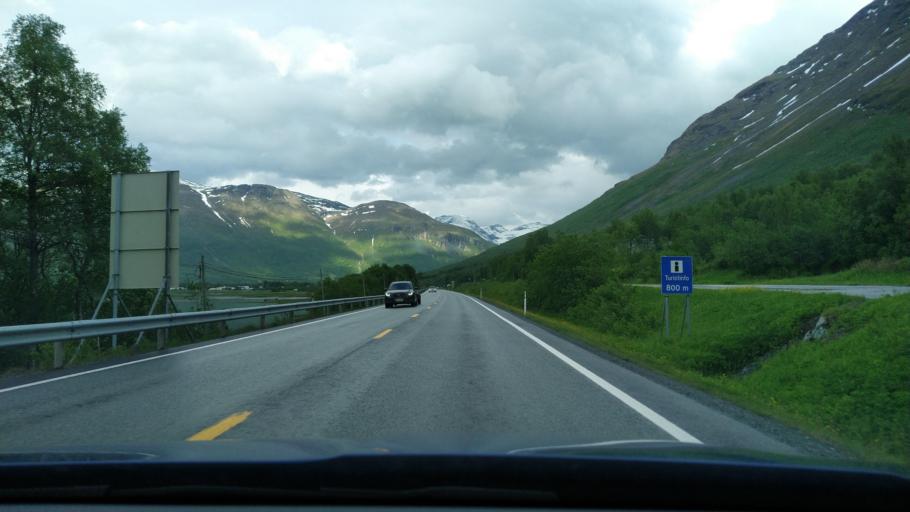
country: NO
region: Troms
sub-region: Balsfjord
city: Storsteinnes
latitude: 69.2142
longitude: 19.5161
